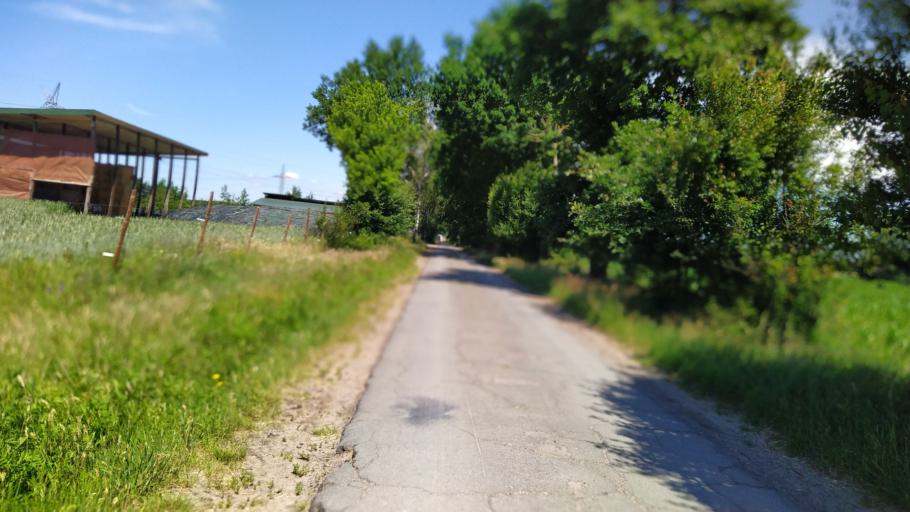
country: DE
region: Lower Saxony
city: Deinste
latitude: 53.5055
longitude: 9.4410
